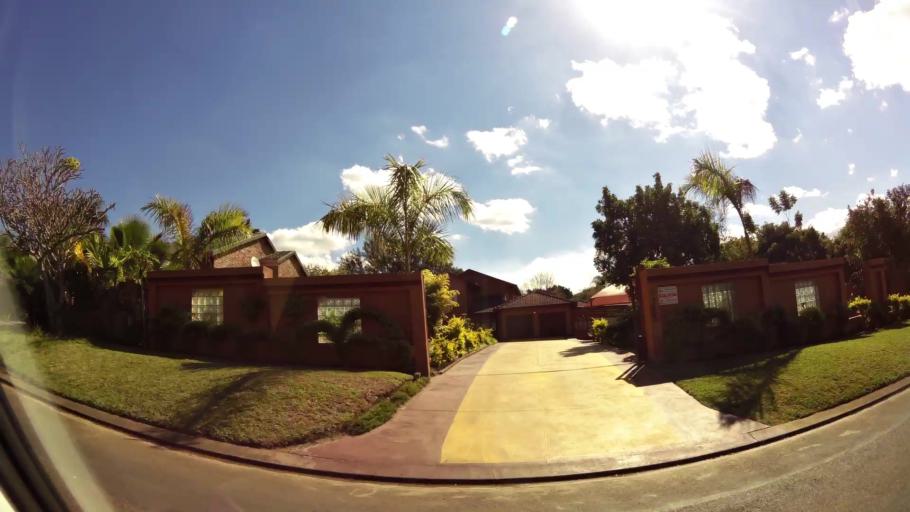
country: ZA
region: Limpopo
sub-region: Mopani District Municipality
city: Tzaneen
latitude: -23.8171
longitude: 30.1550
